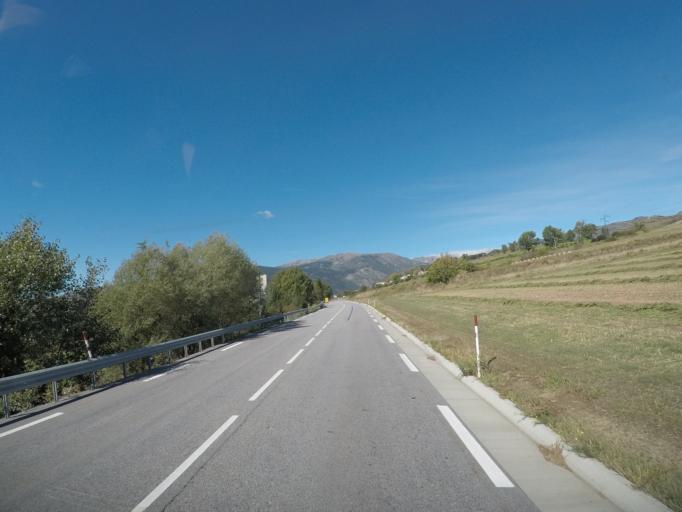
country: ES
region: Catalonia
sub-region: Provincia de Girona
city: Puigcerda
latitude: 42.4563
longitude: 1.9306
